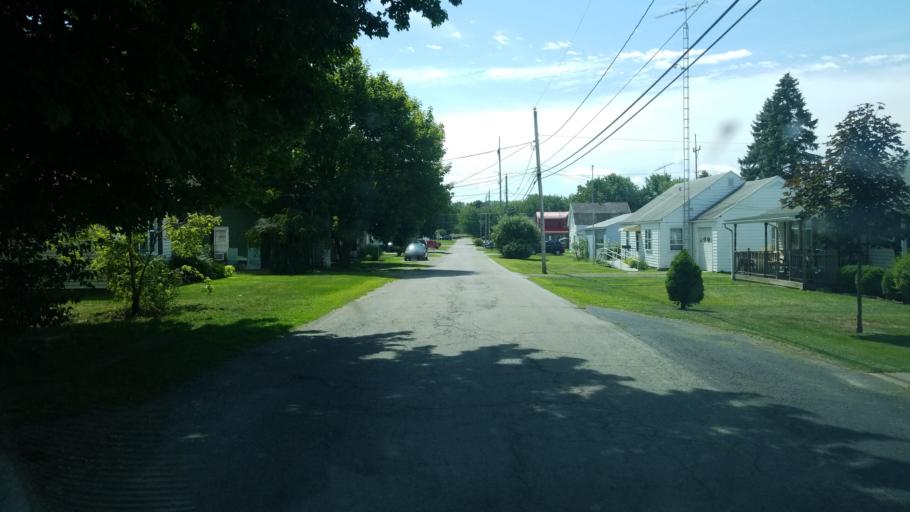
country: US
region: Ohio
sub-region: Hardin County
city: Kenton
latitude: 40.6445
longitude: -83.5996
